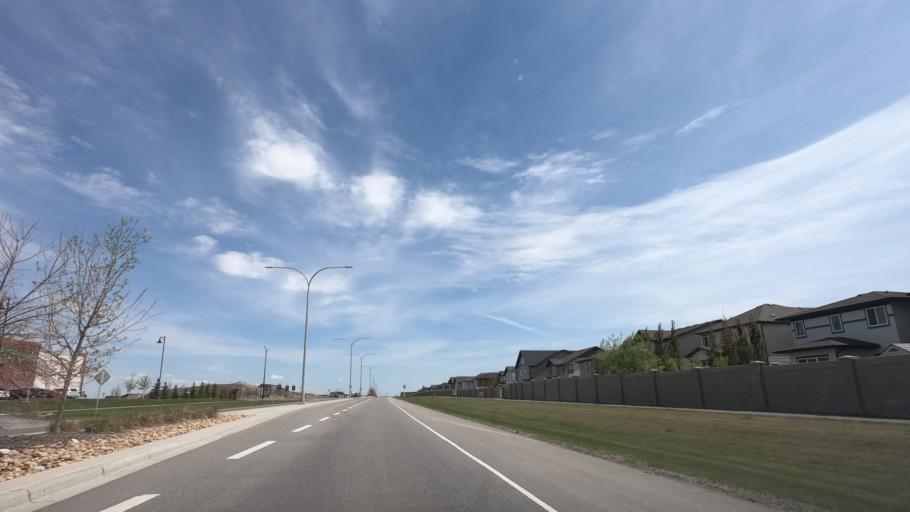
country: CA
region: Alberta
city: Airdrie
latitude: 51.2562
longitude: -114.0224
